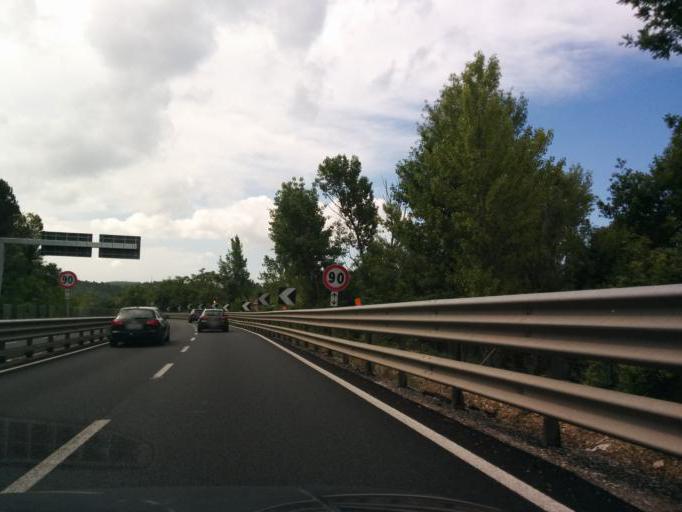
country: IT
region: Tuscany
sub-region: Province of Florence
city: Sambuca
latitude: 43.5490
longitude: 11.2102
